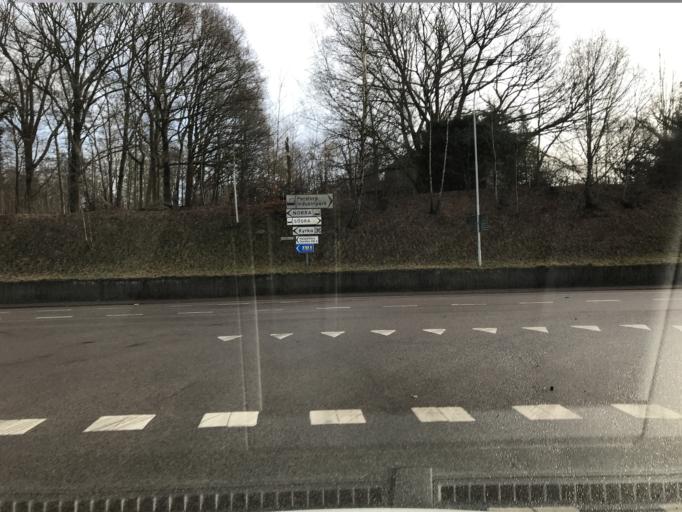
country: SE
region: Skane
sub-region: Perstorps Kommun
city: Perstorp
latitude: 56.1350
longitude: 13.3901
